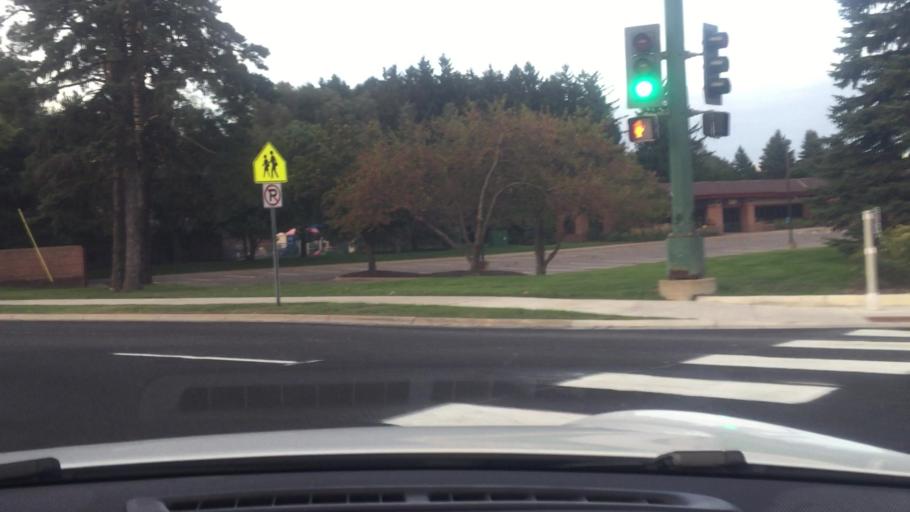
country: US
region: Minnesota
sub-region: Ramsey County
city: Shoreview
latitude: 45.0815
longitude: -93.1181
